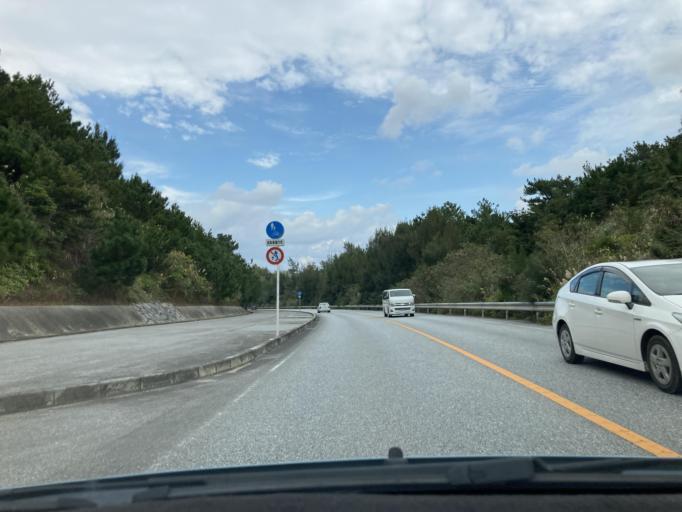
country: JP
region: Okinawa
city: Ishikawa
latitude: 26.4848
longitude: 127.8534
